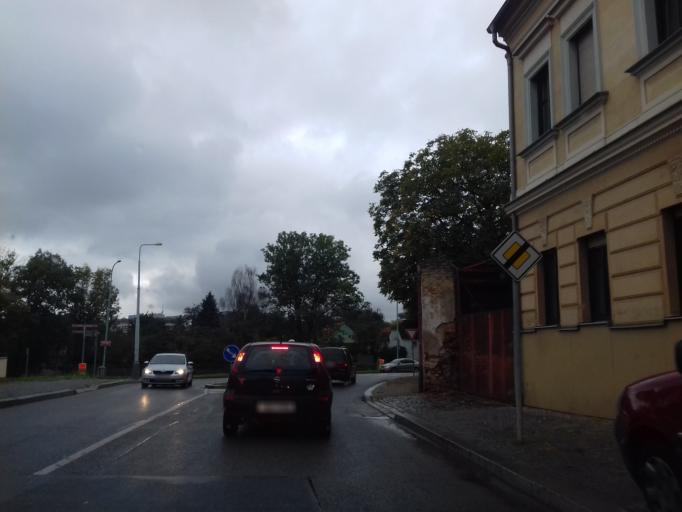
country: CZ
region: Praha
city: Branik
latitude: 50.0532
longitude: 14.3592
